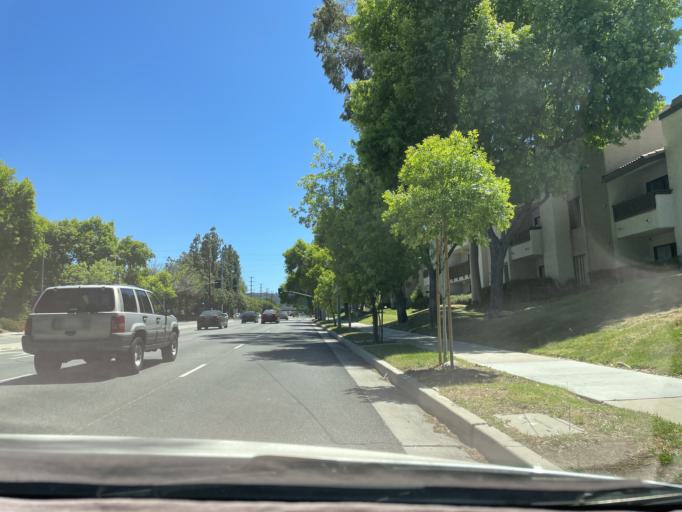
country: US
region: California
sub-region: Los Angeles County
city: Woodland Hills
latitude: 34.1744
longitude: -118.5975
